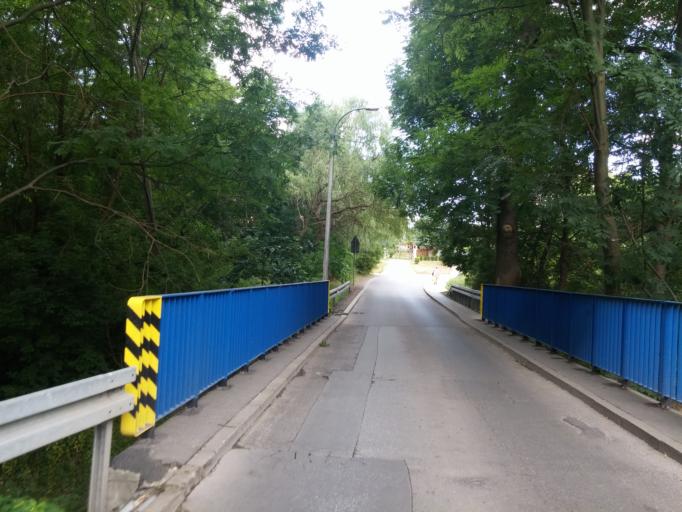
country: PL
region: Lesser Poland Voivodeship
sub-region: Powiat krakowski
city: Ochojno
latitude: 50.0150
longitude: 19.9846
